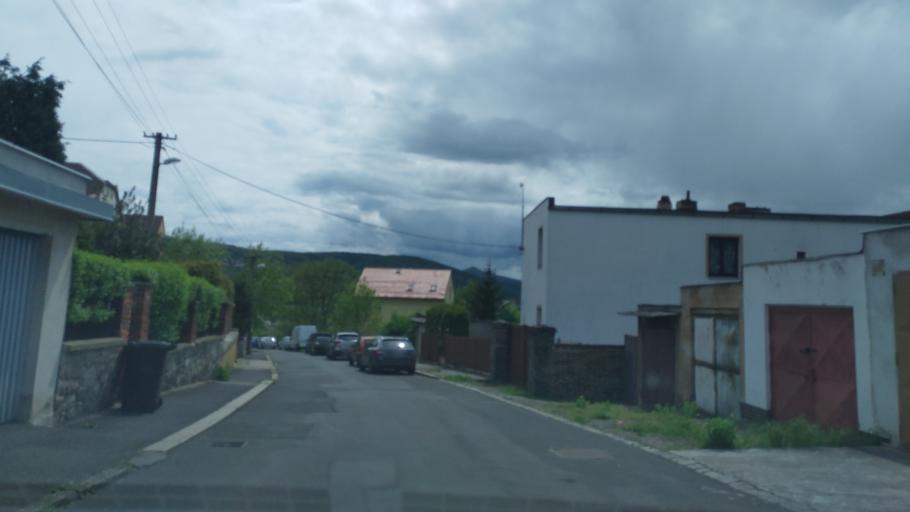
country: CZ
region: Ustecky
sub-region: Okres Usti nad Labem
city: Usti nad Labem
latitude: 50.6629
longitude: 14.0123
